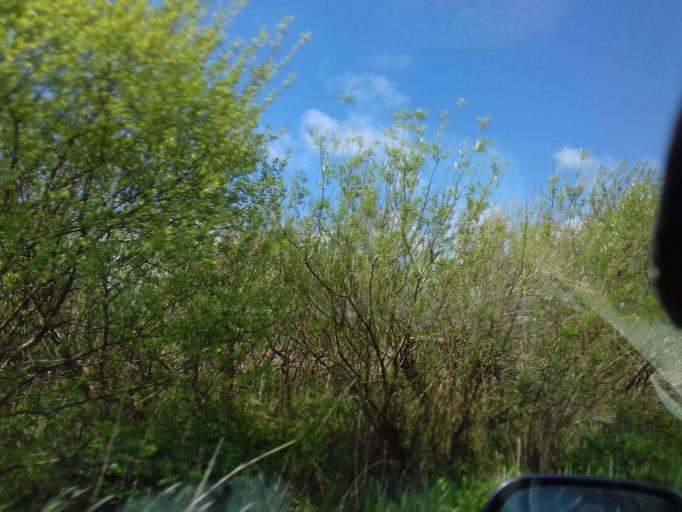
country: IE
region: Leinster
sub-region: Loch Garman
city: Castlebridge
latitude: 52.3890
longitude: -6.3680
